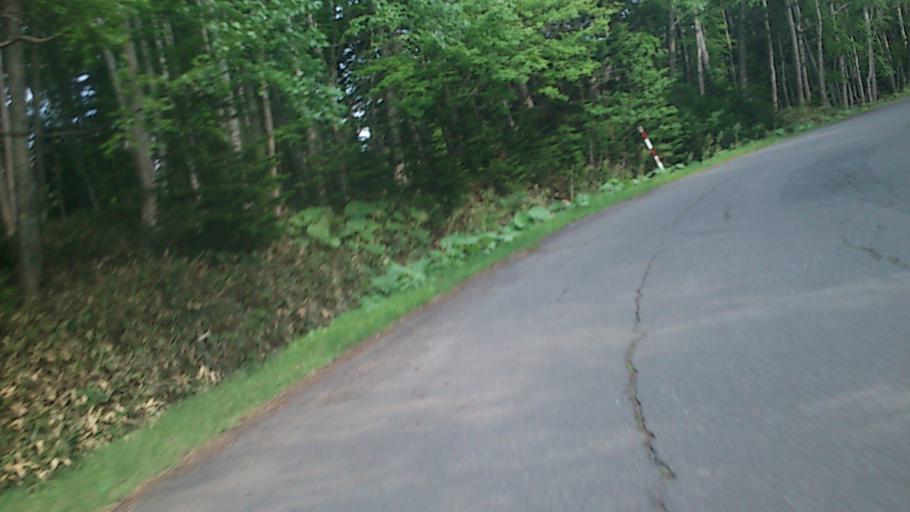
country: JP
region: Hokkaido
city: Bihoro
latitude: 43.4296
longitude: 144.0841
